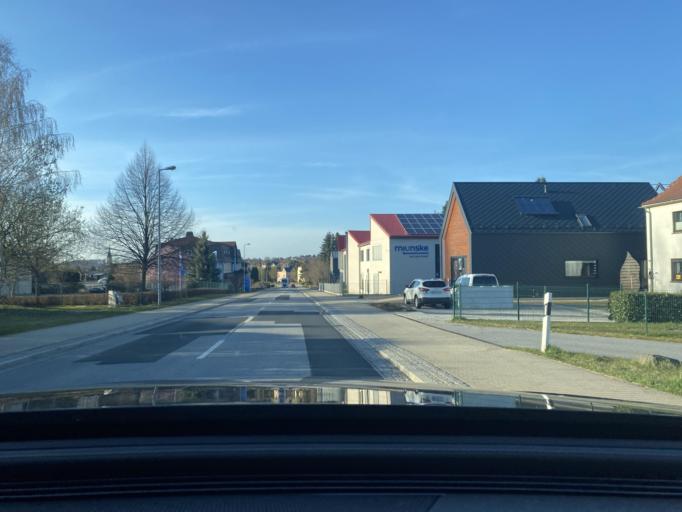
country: DE
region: Saxony
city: Grosspostwitz
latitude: 51.1114
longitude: 14.4459
